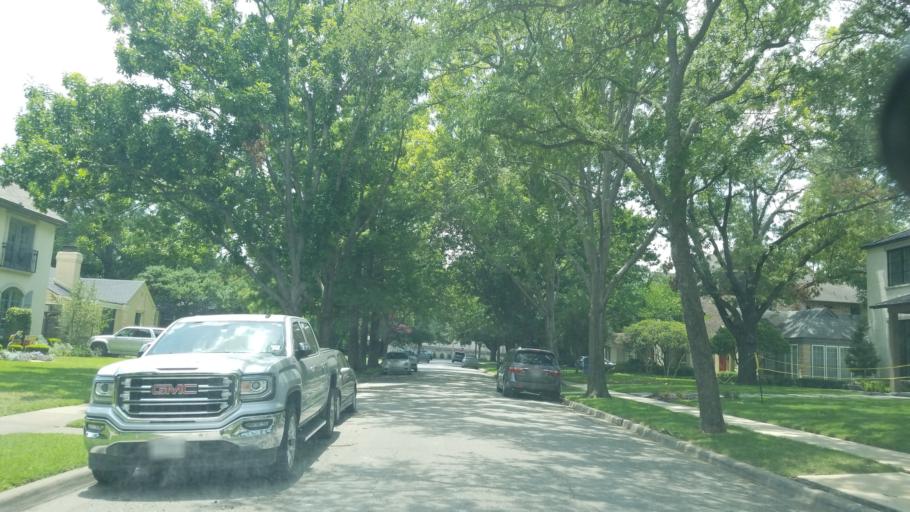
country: US
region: Texas
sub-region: Dallas County
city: University Park
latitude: 32.8522
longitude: -96.8110
